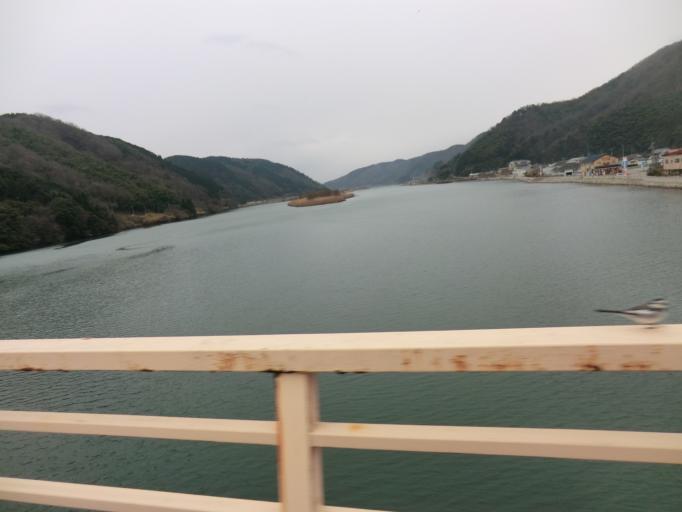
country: JP
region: Hyogo
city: Toyooka
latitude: 35.6077
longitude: 134.8041
